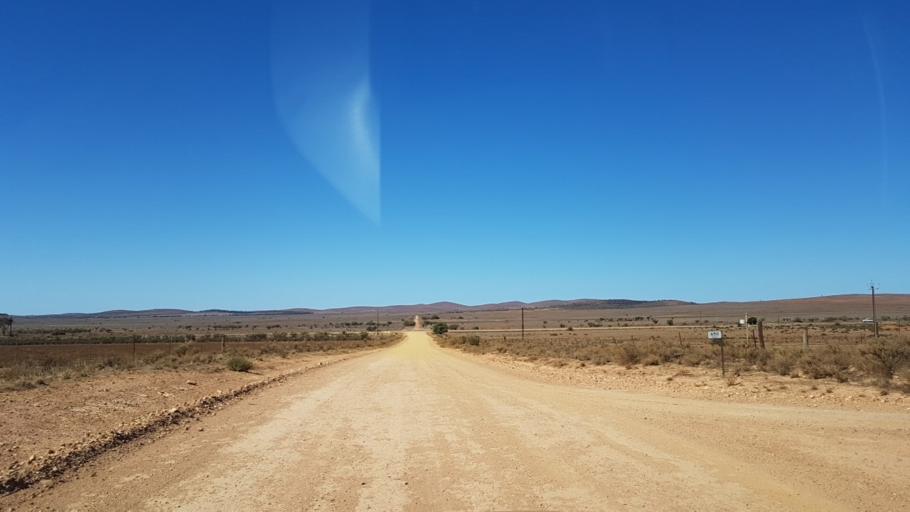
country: AU
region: South Australia
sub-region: Peterborough
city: Peterborough
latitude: -32.9905
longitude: 138.8449
